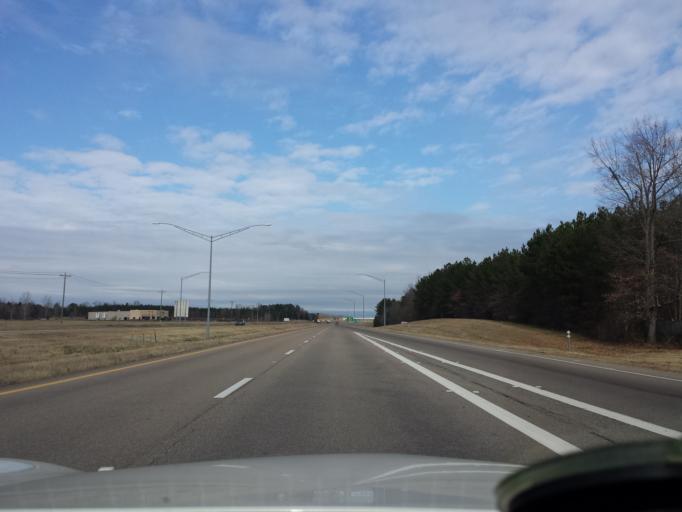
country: US
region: Mississippi
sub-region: Oktibbeha County
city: Starkville
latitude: 33.4463
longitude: -88.8537
